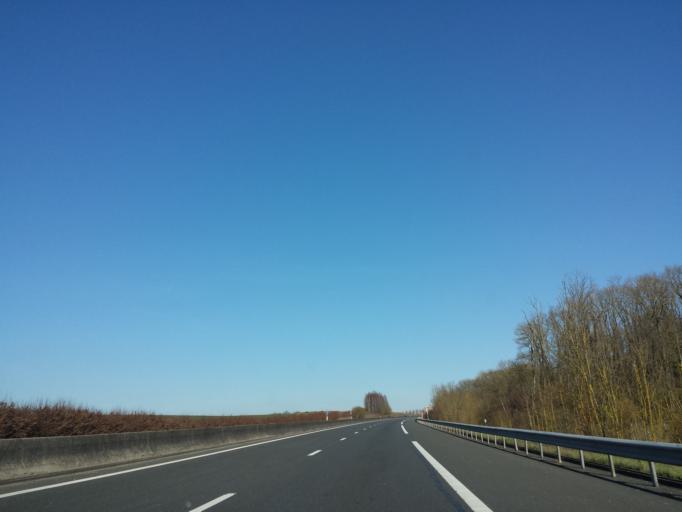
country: FR
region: Picardie
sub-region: Departement de l'Oise
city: Breteuil
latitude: 49.5861
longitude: 2.2033
